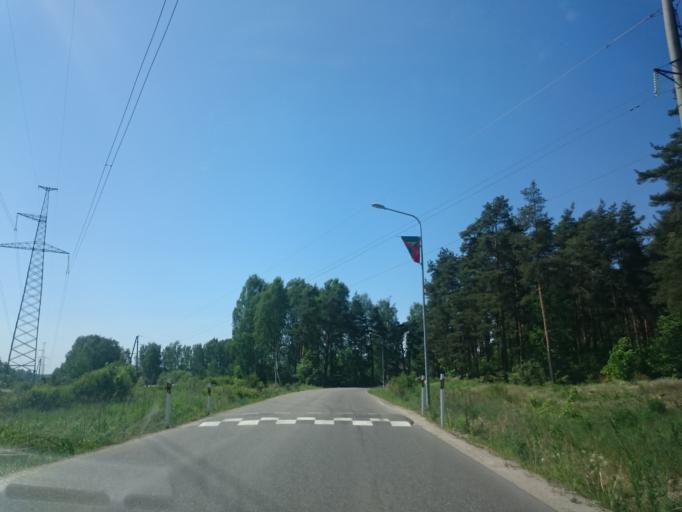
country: LV
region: Kekava
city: Balozi
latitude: 56.8632
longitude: 24.0821
